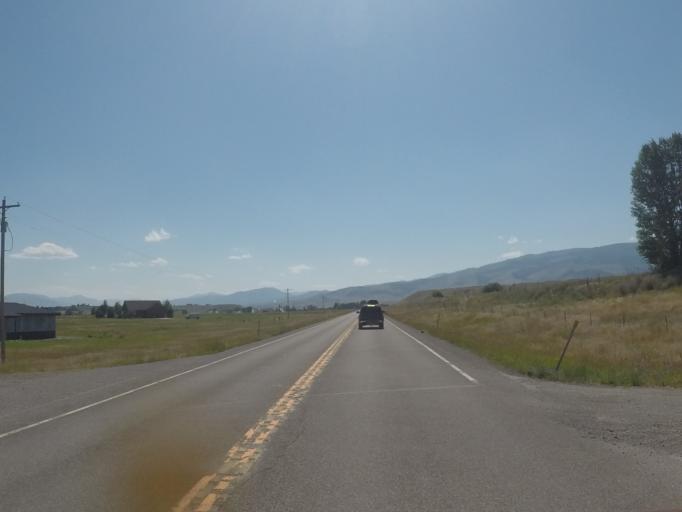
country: US
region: Montana
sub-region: Park County
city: Livingston
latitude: 45.4249
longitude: -110.6509
